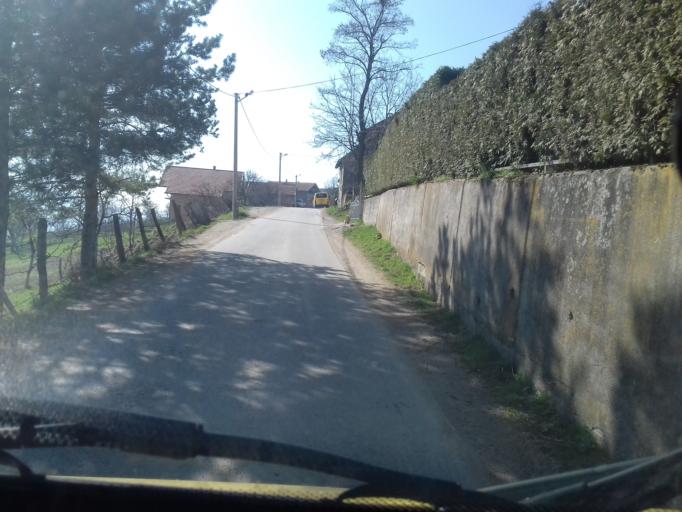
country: BA
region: Federation of Bosnia and Herzegovina
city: Travnik
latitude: 44.2526
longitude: 17.7348
